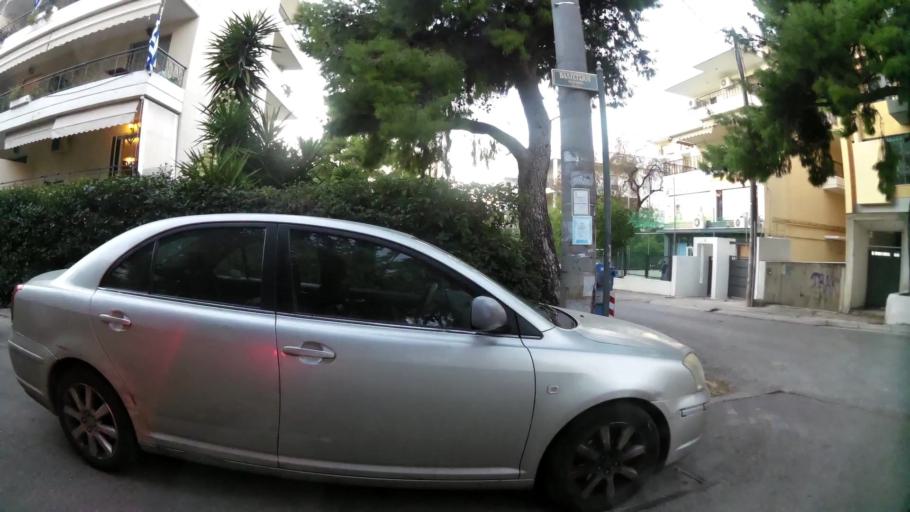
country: GR
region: Attica
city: Pefki
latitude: 38.0624
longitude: 23.7978
